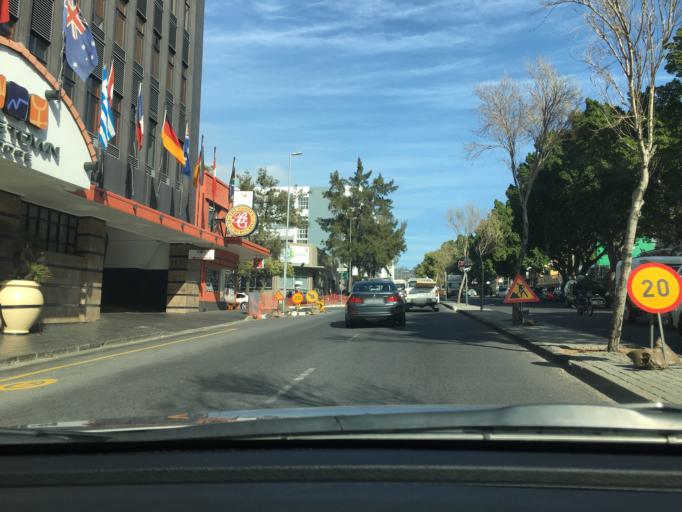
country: ZA
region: Western Cape
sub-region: City of Cape Town
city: Cape Town
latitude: -33.9222
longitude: 18.4158
